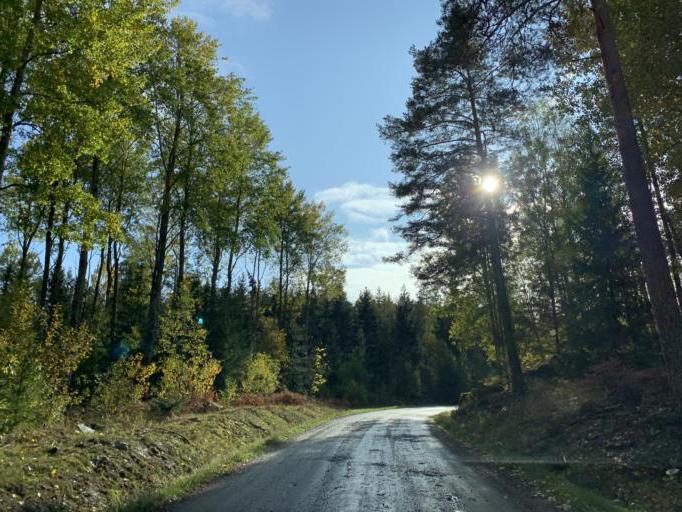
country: SE
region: Soedermanland
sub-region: Eskilstuna Kommun
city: Kvicksund
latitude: 59.3673
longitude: 16.2640
